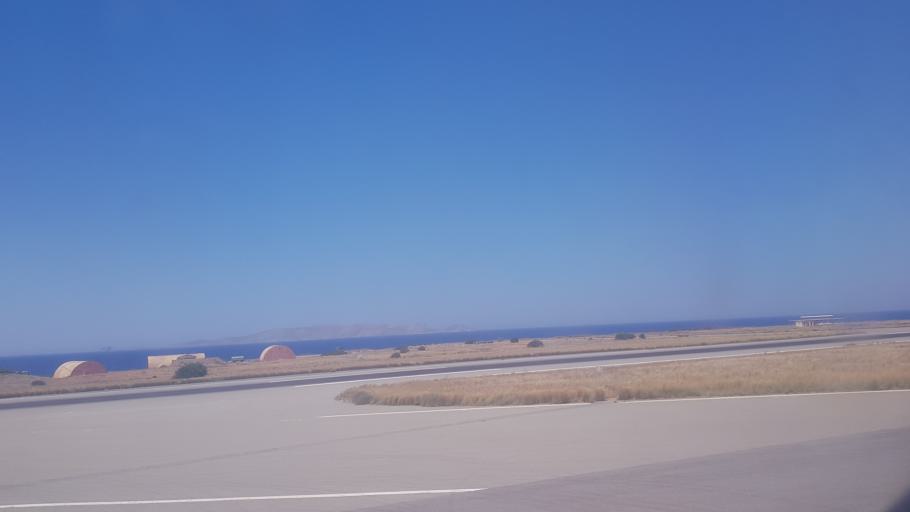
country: GR
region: Crete
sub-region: Nomos Irakleiou
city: Nea Alikarnassos
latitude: 35.3387
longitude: 25.1815
